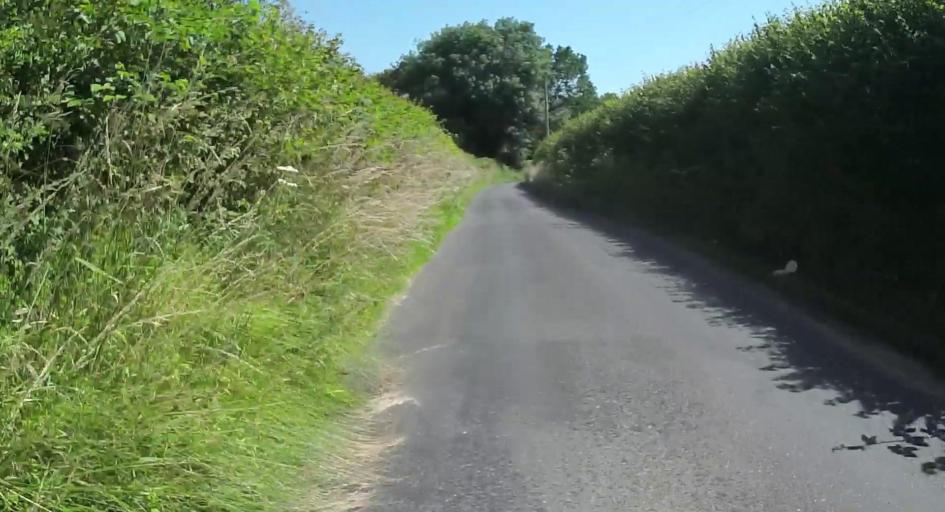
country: GB
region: England
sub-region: Surrey
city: Churt
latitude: 51.1549
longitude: -0.8098
